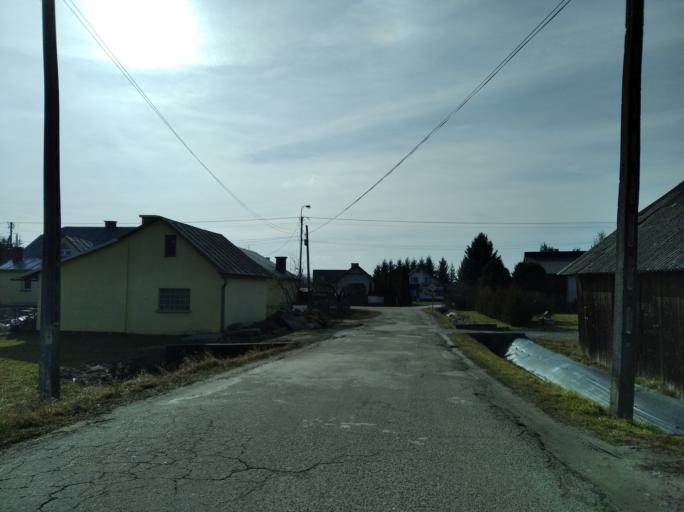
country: PL
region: Subcarpathian Voivodeship
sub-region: Powiat brzozowski
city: Humniska
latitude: 49.6698
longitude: 22.0535
